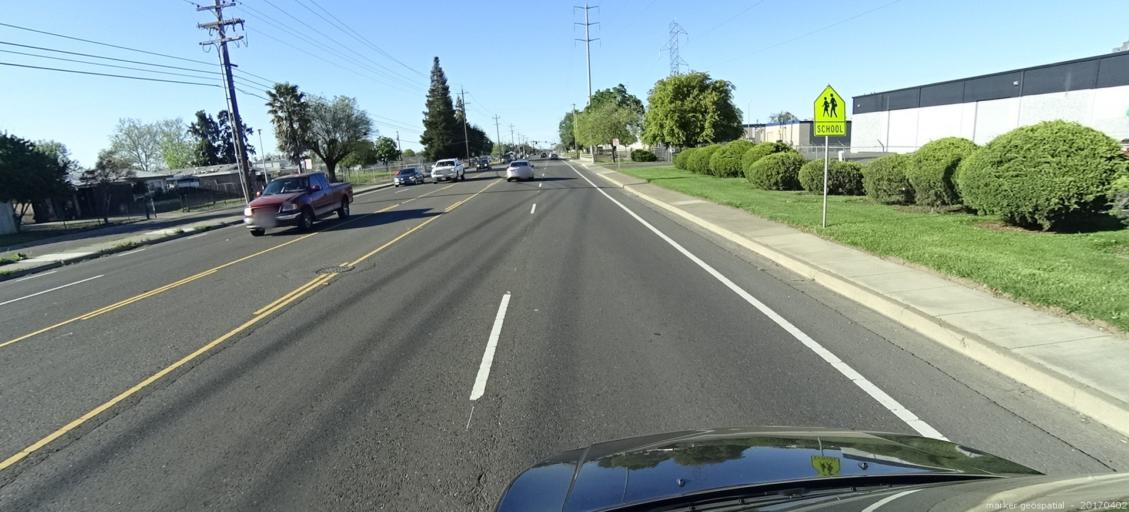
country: US
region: California
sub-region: Sacramento County
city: Florin
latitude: 38.5137
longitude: -121.4090
